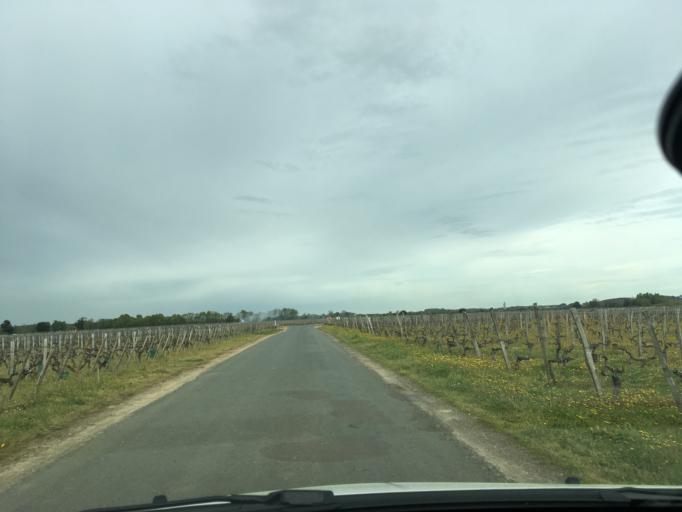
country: FR
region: Aquitaine
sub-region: Departement de la Gironde
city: Lesparre-Medoc
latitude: 45.3254
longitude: -0.8821
